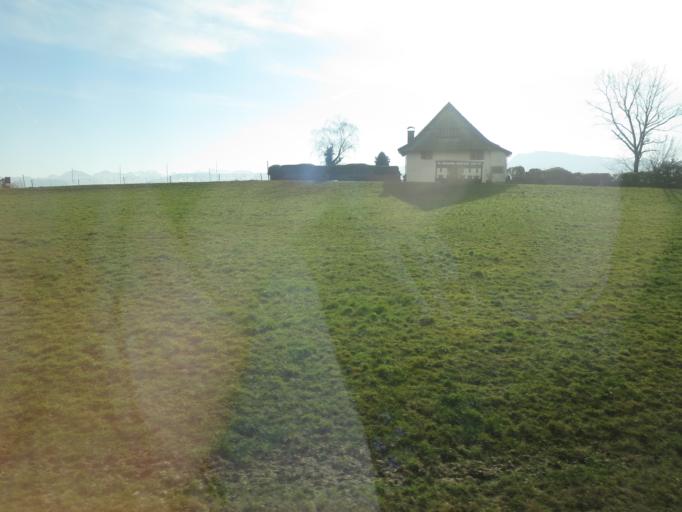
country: CH
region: Zurich
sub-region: Bezirk Meilen
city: Uerikon
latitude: 47.2357
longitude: 8.7689
